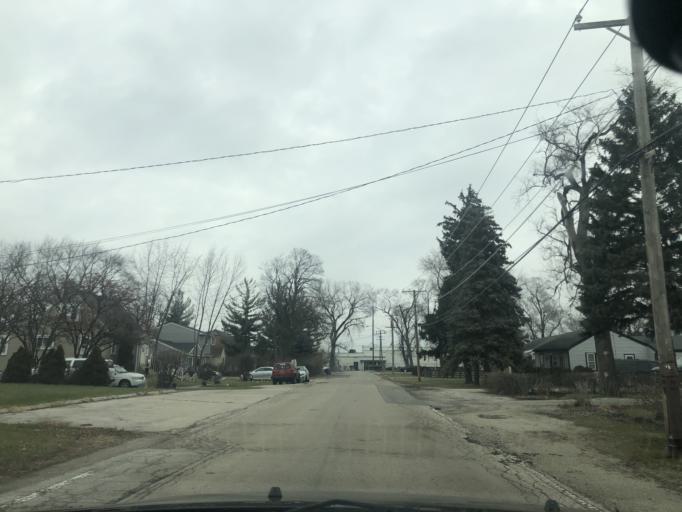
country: US
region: Illinois
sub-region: Cook County
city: Northlake
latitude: 41.9346
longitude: -87.8970
